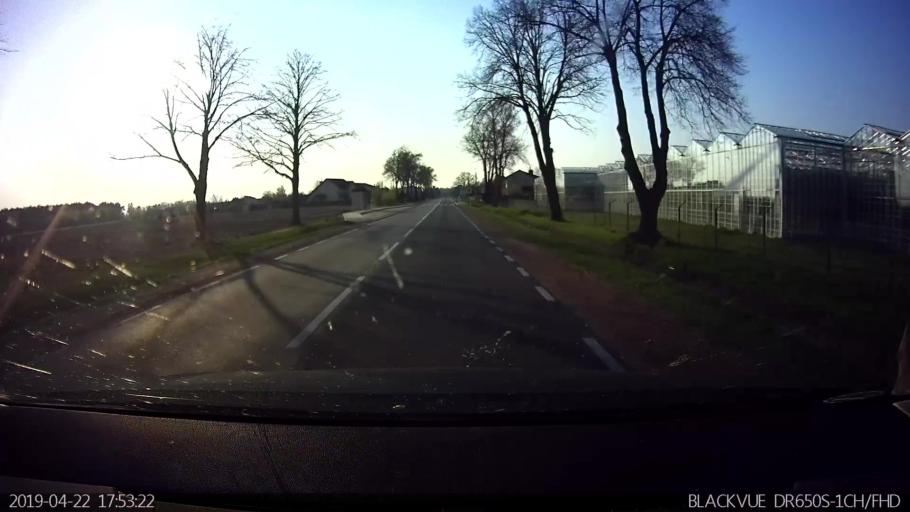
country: PL
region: Masovian Voivodeship
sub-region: Powiat wegrowski
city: Liw
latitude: 52.4524
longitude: 21.9557
